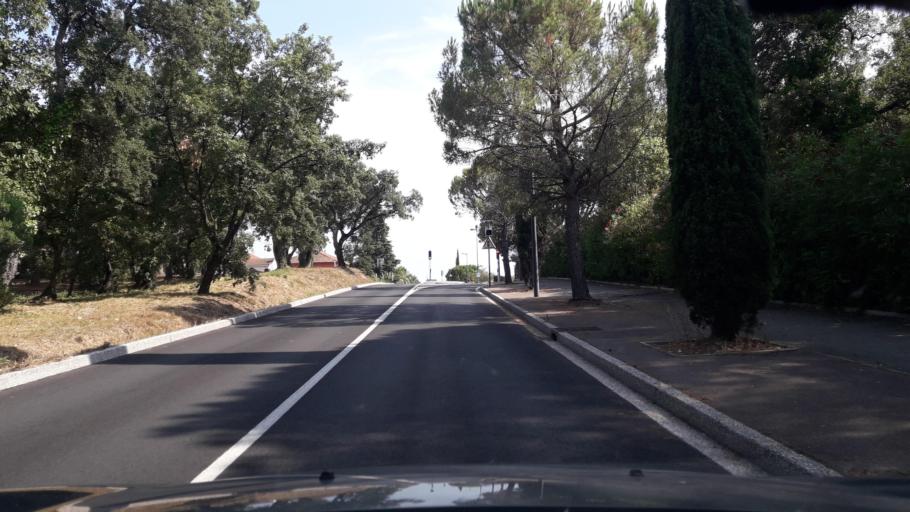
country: FR
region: Provence-Alpes-Cote d'Azur
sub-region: Departement du Var
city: Frejus
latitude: 43.4485
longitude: 6.7485
